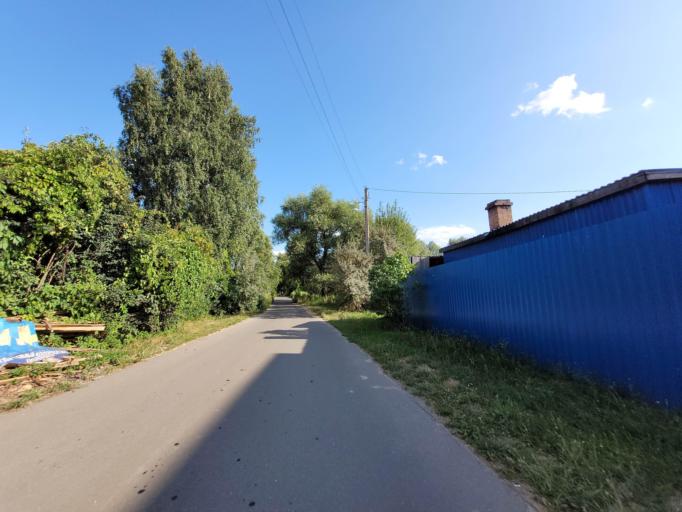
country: RU
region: Moskovskaya
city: Konobeyevo
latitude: 55.4136
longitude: 38.6944
